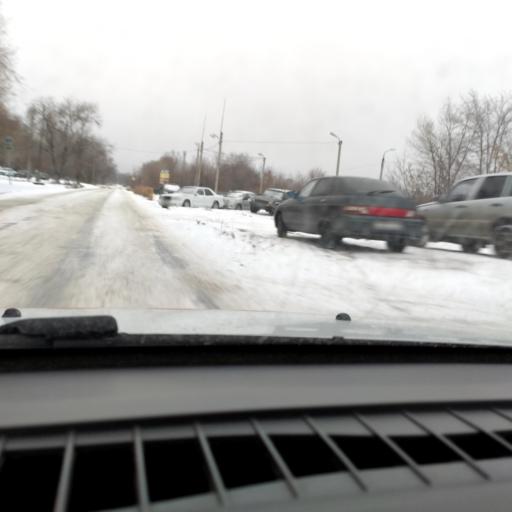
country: RU
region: Samara
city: Tol'yatti
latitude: 53.5579
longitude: 49.3005
